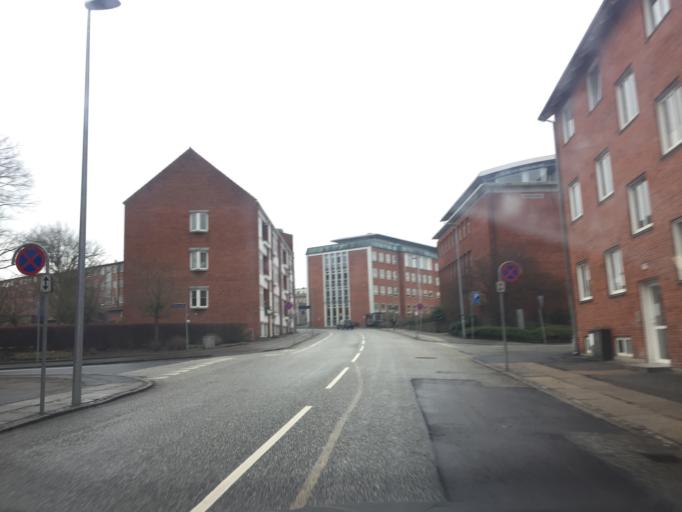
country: DK
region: Zealand
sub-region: Slagelse Kommune
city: Slagelse
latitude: 55.4066
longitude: 11.3568
